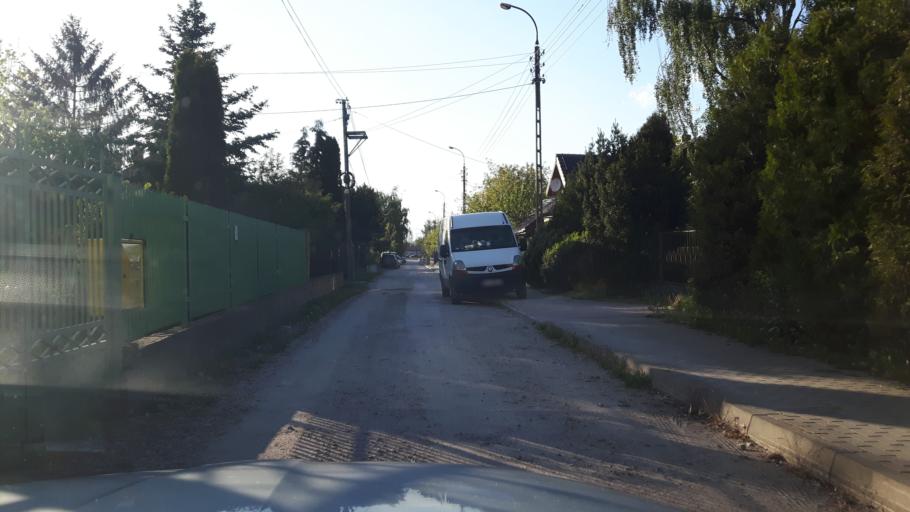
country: PL
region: Masovian Voivodeship
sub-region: Warszawa
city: Targowek
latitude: 52.2752
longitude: 21.0705
